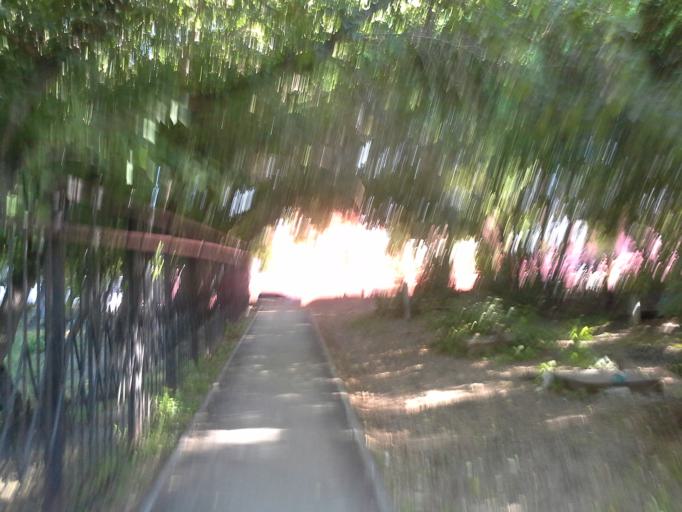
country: RU
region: Novosibirsk
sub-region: Novosibirskiy Rayon
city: Novosibirsk
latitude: 54.9846
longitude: 82.9086
